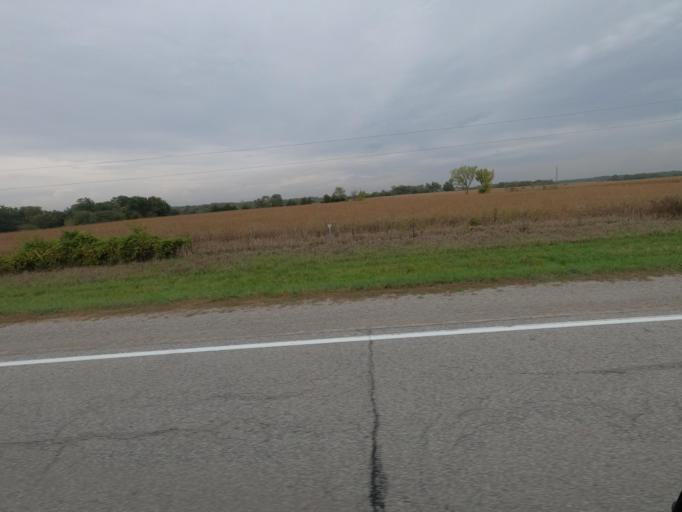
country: US
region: Iowa
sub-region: Van Buren County
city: Keosauqua
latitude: 40.8539
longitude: -92.0555
